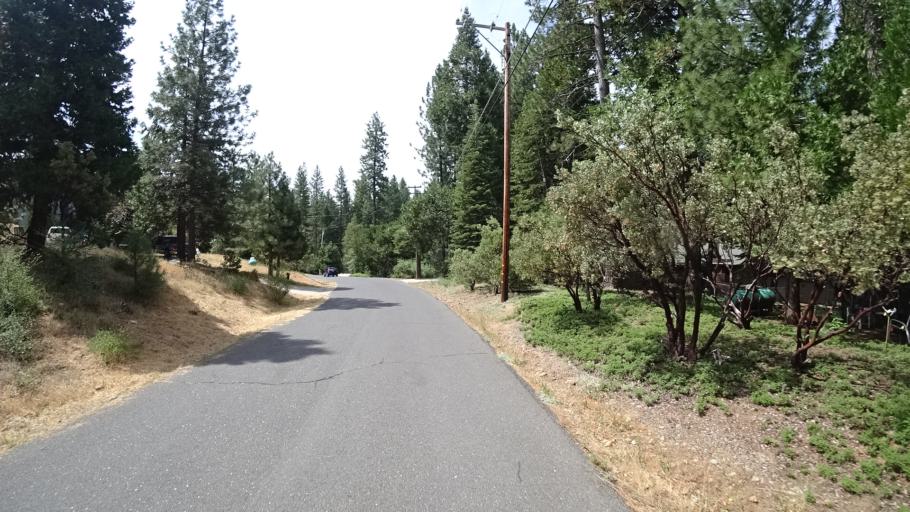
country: US
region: California
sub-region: Calaveras County
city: Arnold
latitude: 38.2489
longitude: -120.3559
